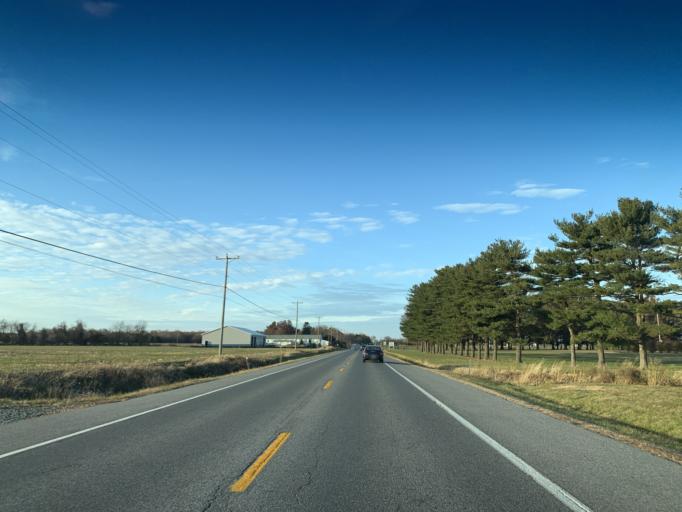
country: US
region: Maryland
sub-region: Kent County
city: Chestertown
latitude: 39.2758
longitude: -76.0925
